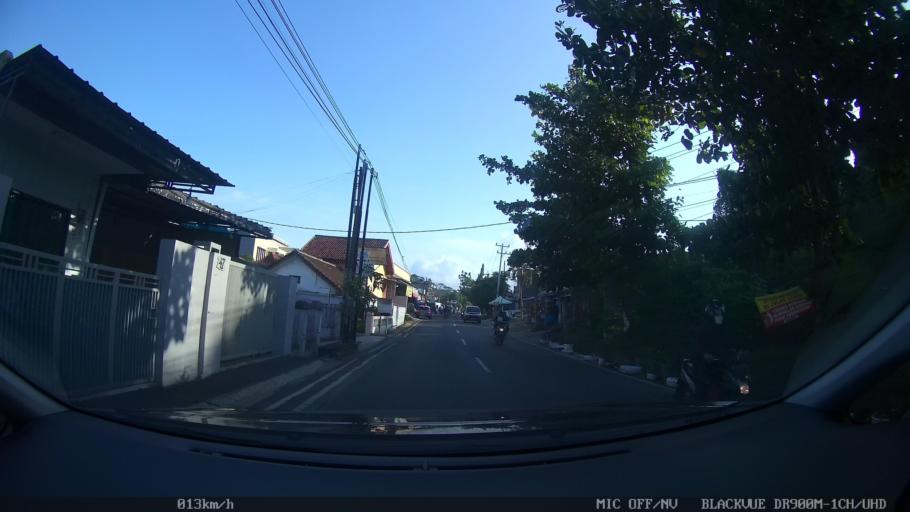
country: ID
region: Lampung
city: Bandarlampung
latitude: -5.4073
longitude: 105.2490
